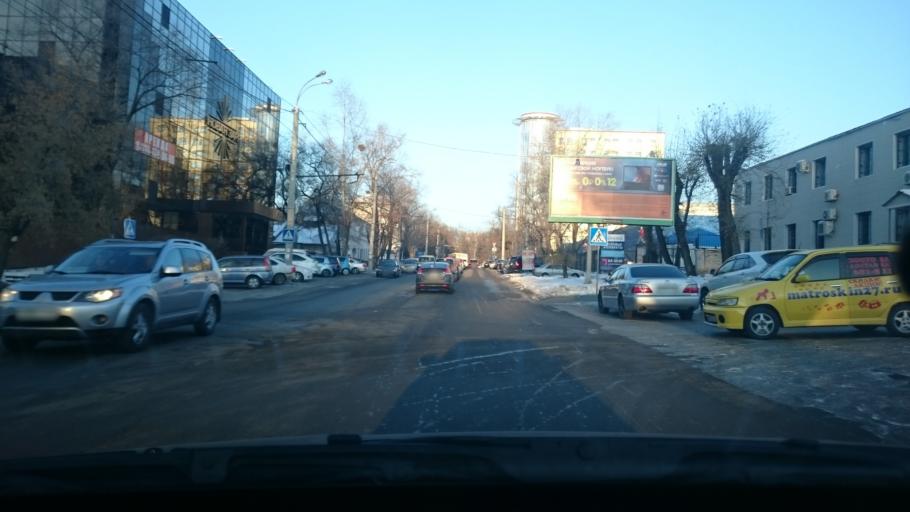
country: RU
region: Khabarovsk Krai
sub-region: Khabarovskiy Rayon
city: Khabarovsk
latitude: 48.4904
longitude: 135.0817
